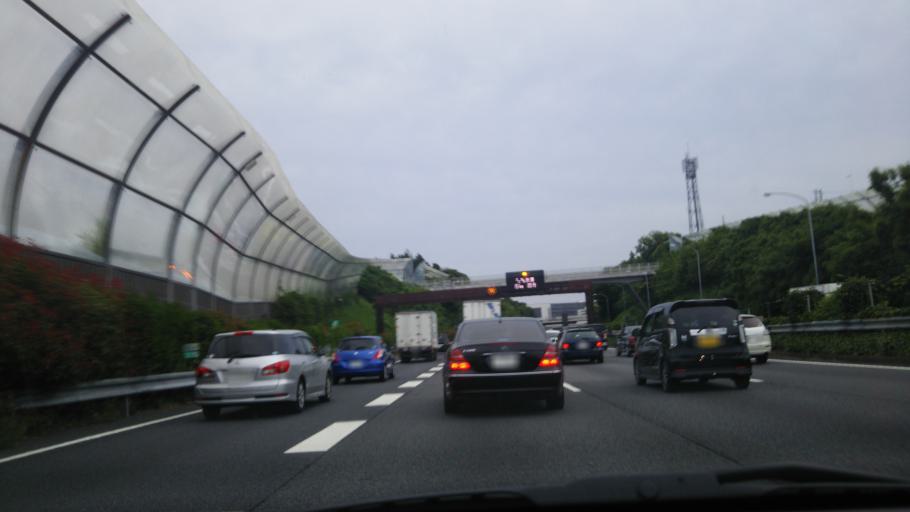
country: JP
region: Kanagawa
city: Atsugi
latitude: 35.4384
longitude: 139.4054
